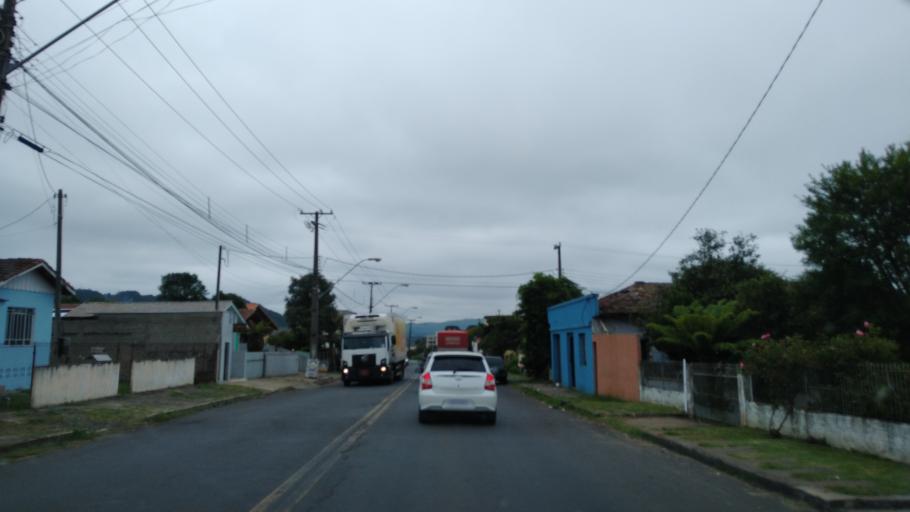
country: BR
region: Santa Catarina
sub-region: Porto Uniao
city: Porto Uniao
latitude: -26.2545
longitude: -51.0885
